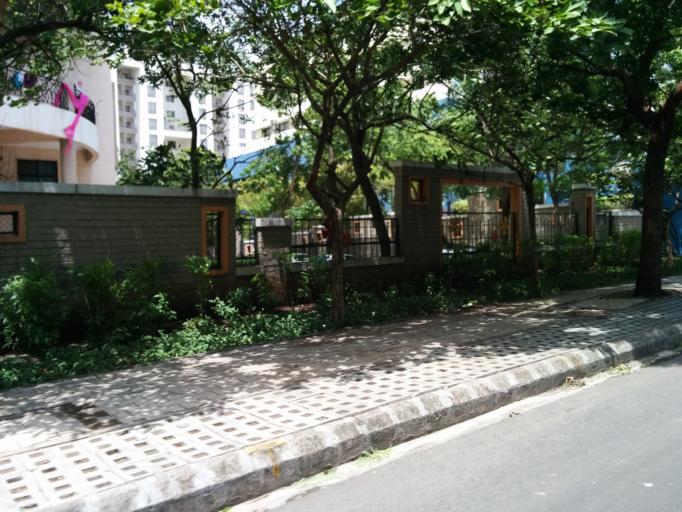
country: IN
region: Maharashtra
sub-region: Pune Division
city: Pune
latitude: 18.5103
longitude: 73.9291
